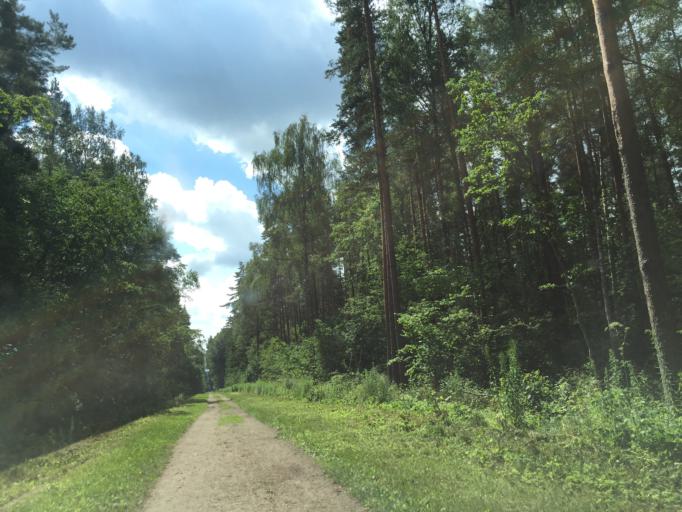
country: LV
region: Ozolnieku
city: Ozolnieki
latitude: 56.6786
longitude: 23.7531
